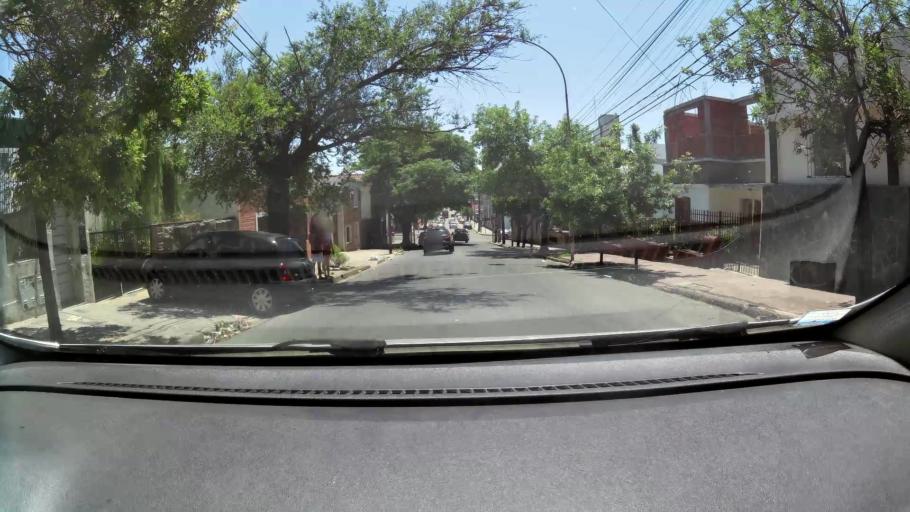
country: AR
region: Cordoba
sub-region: Departamento de Capital
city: Cordoba
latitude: -31.4043
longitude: -64.2124
